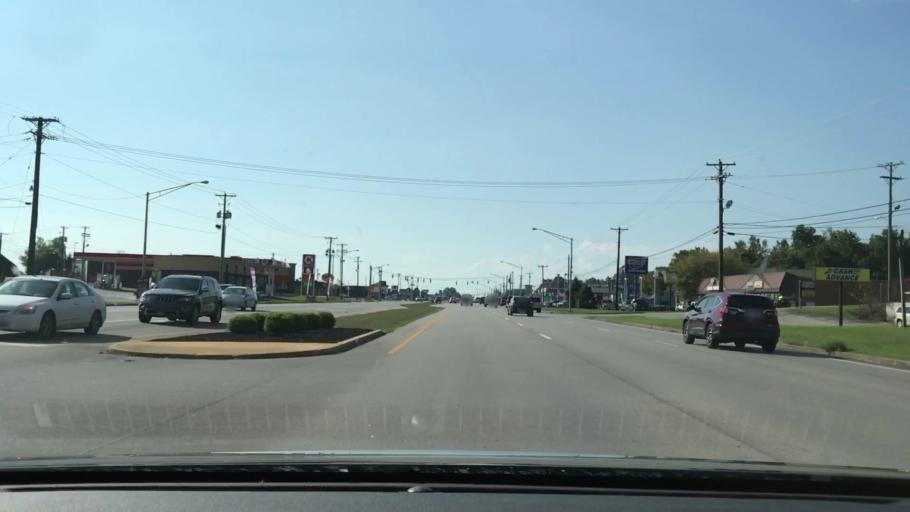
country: US
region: Kentucky
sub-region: Pulaski County
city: Somerset
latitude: 37.0818
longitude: -84.6172
